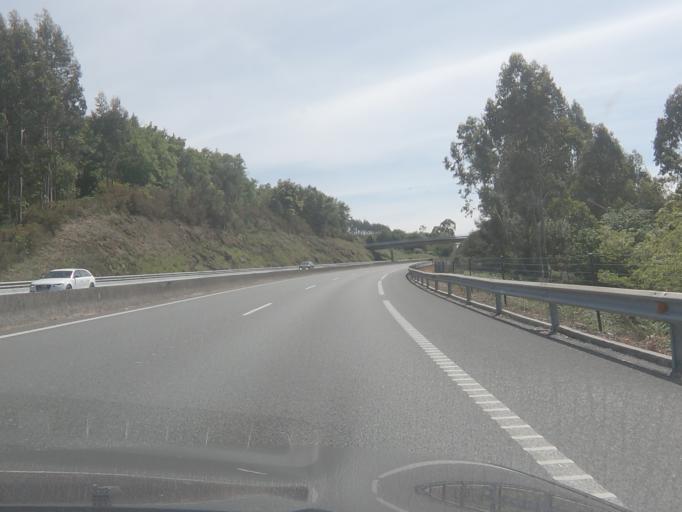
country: ES
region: Galicia
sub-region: Provincia da Coruna
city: Padron
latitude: 42.7759
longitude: -8.6420
